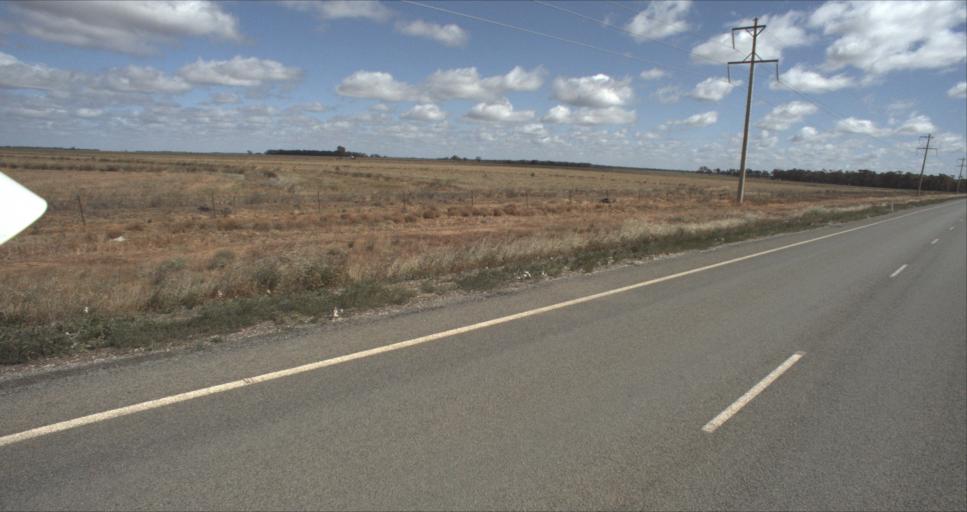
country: AU
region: New South Wales
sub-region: Murrumbidgee Shire
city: Darlington Point
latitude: -34.5824
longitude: 146.1648
